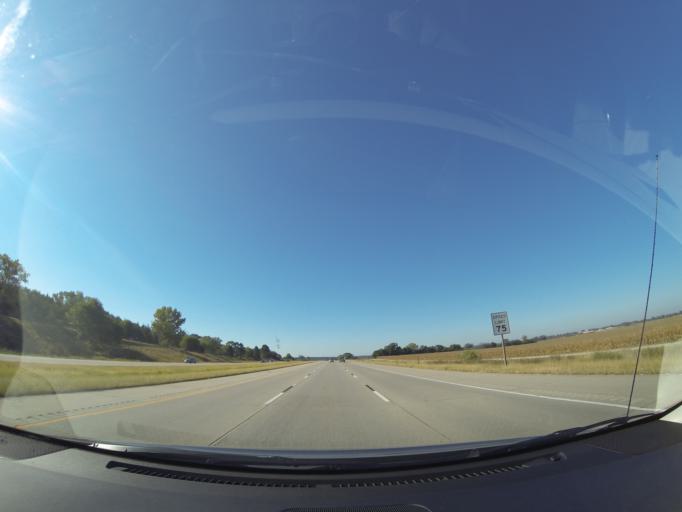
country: US
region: Nebraska
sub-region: Saunders County
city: Ashland
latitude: 41.0689
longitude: -96.2881
